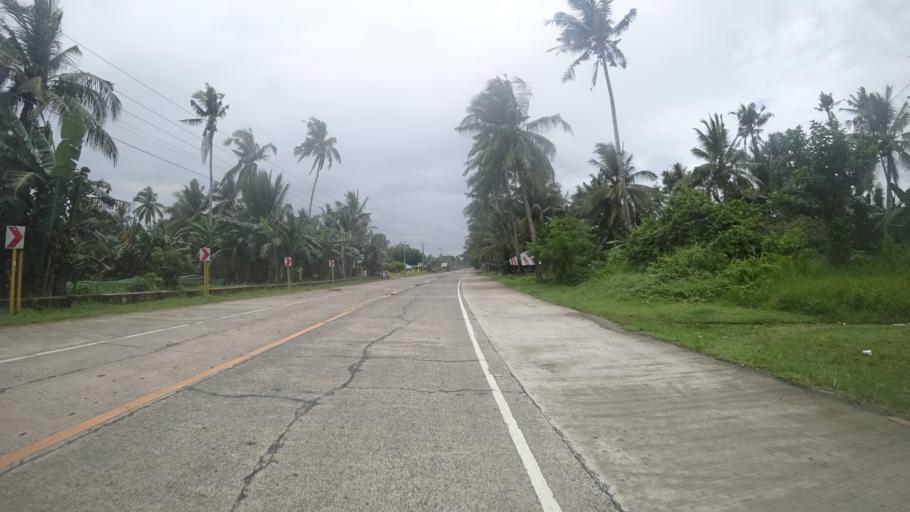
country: PH
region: Eastern Visayas
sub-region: Province of Leyte
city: MacArthur
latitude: 10.8465
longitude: 124.9948
